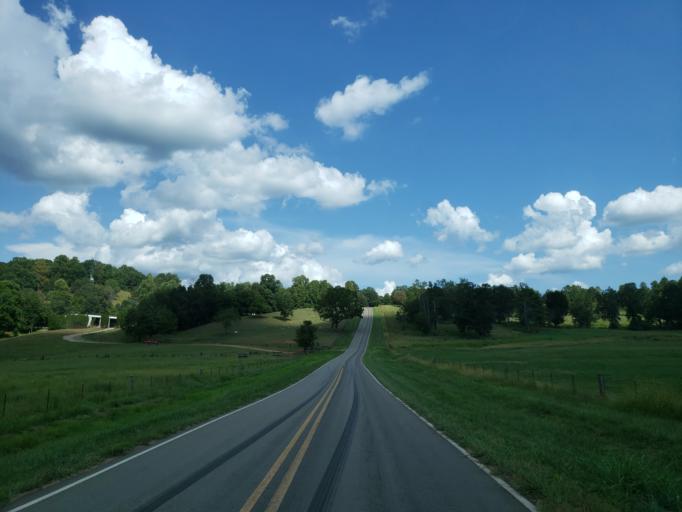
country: US
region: Georgia
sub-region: Pickens County
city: Jasper
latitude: 34.4167
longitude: -84.4548
